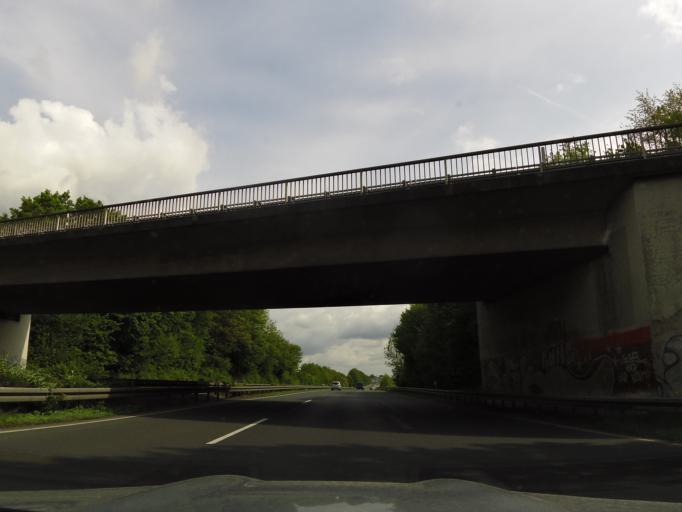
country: DE
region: Hesse
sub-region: Regierungsbezirk Giessen
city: Dehrn
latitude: 50.4389
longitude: 8.0956
